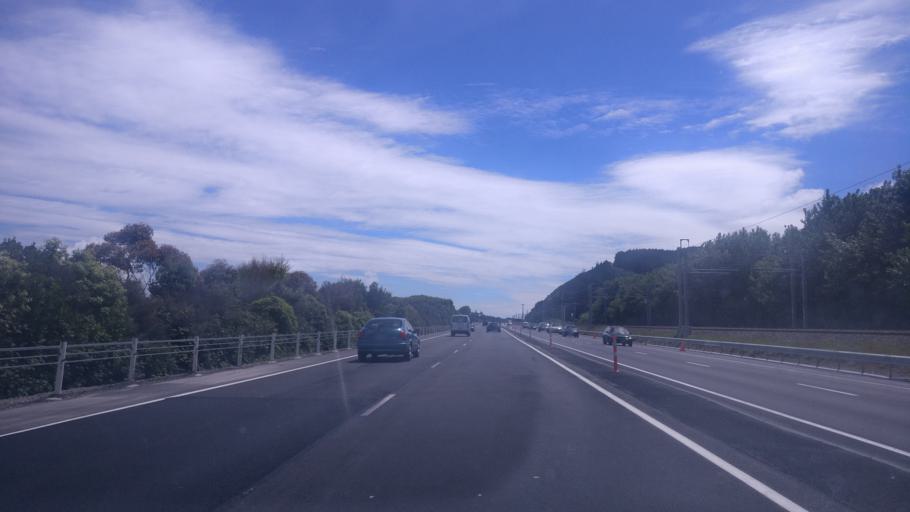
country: NZ
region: Wellington
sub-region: Kapiti Coast District
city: Paraparaumu
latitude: -40.9597
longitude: 174.9874
